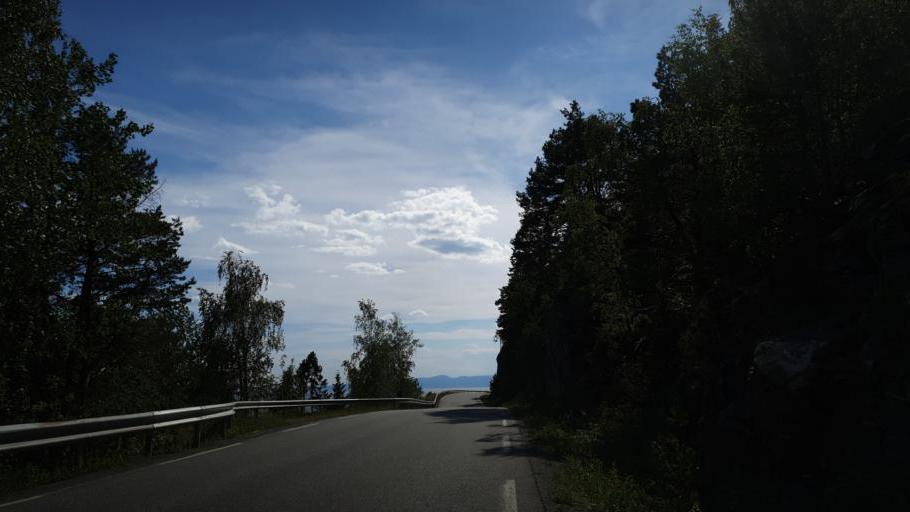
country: NO
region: Nord-Trondelag
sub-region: Leksvik
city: Leksvik
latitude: 63.6301
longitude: 10.5676
